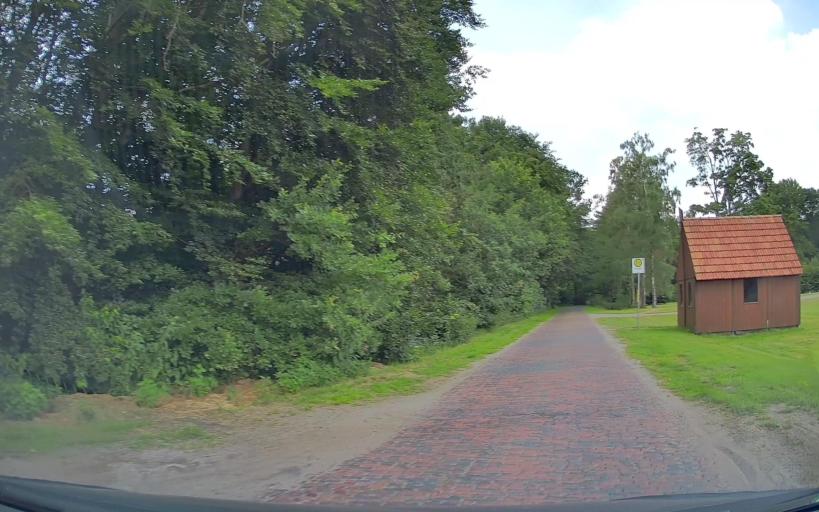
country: DE
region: Lower Saxony
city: Friesoythe
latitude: 52.9805
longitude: 7.8908
